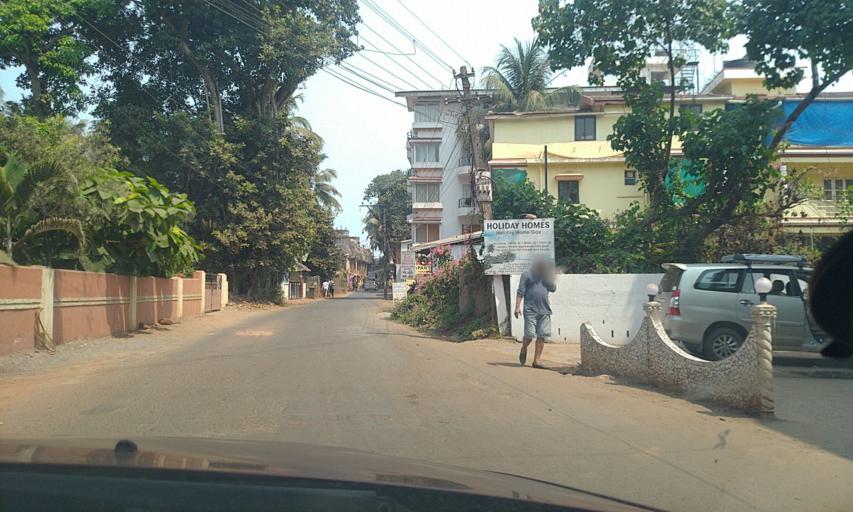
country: IN
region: Goa
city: Calangute
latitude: 15.5381
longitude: 73.7634
